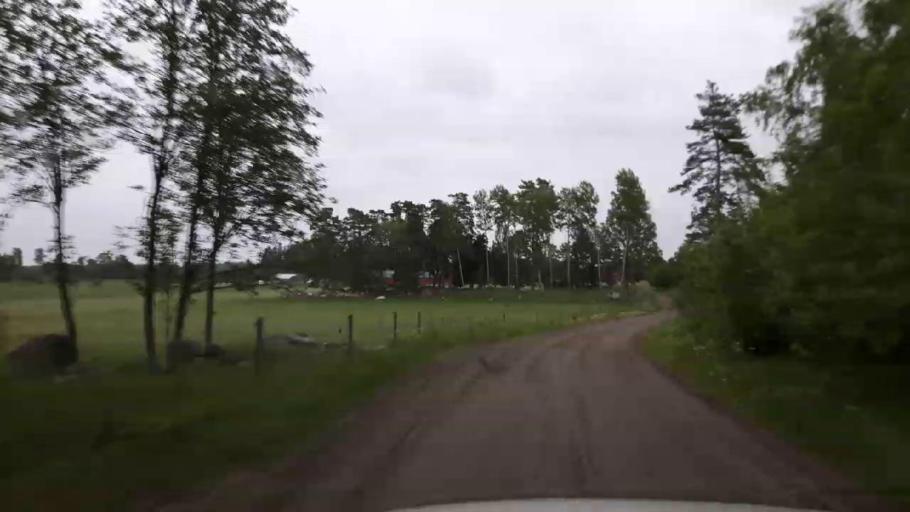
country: SE
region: Soedermanland
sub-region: Eskilstuna Kommun
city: Kvicksund
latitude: 59.4203
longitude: 16.2155
